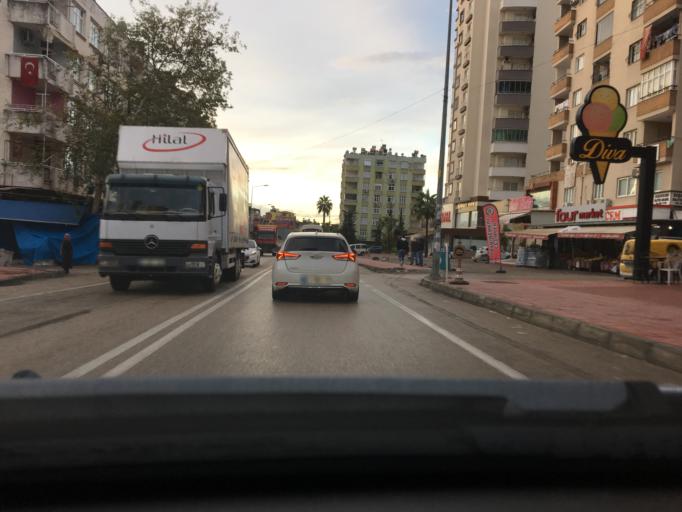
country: TR
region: Adana
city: Seyhan
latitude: 37.0245
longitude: 35.2916
